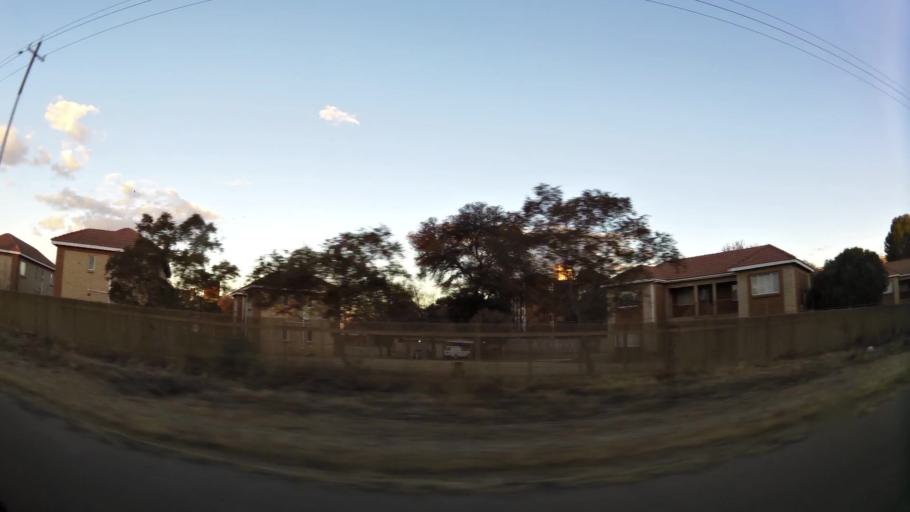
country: ZA
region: North-West
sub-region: Dr Kenneth Kaunda District Municipality
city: Potchefstroom
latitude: -26.6869
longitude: 27.0885
